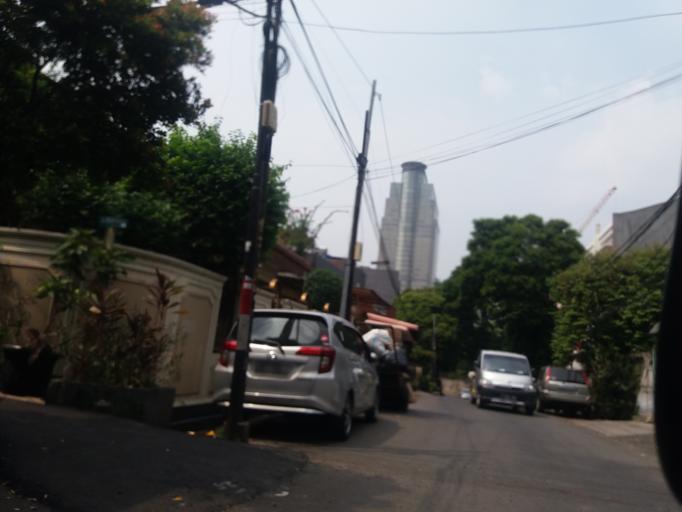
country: ID
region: Jakarta Raya
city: Jakarta
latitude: -6.1905
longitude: 106.8196
